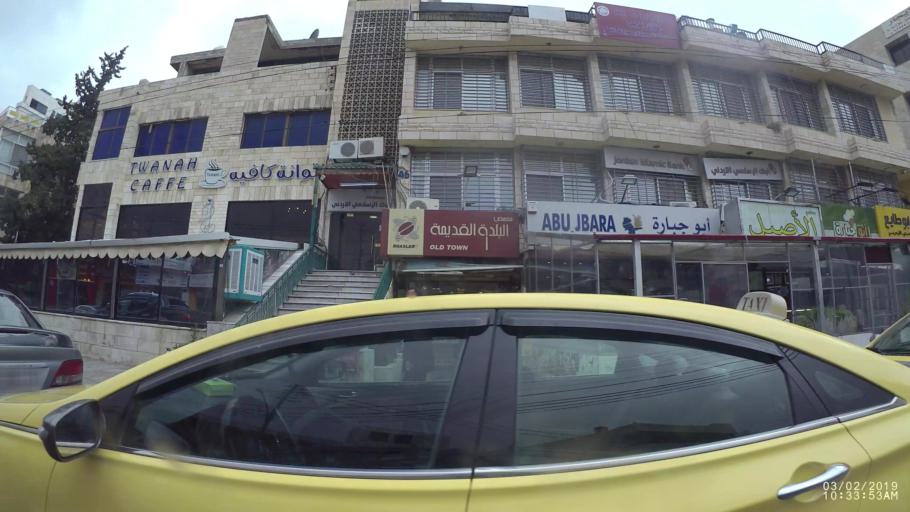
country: JO
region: Amman
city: Amman
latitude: 31.9500
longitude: 35.9169
